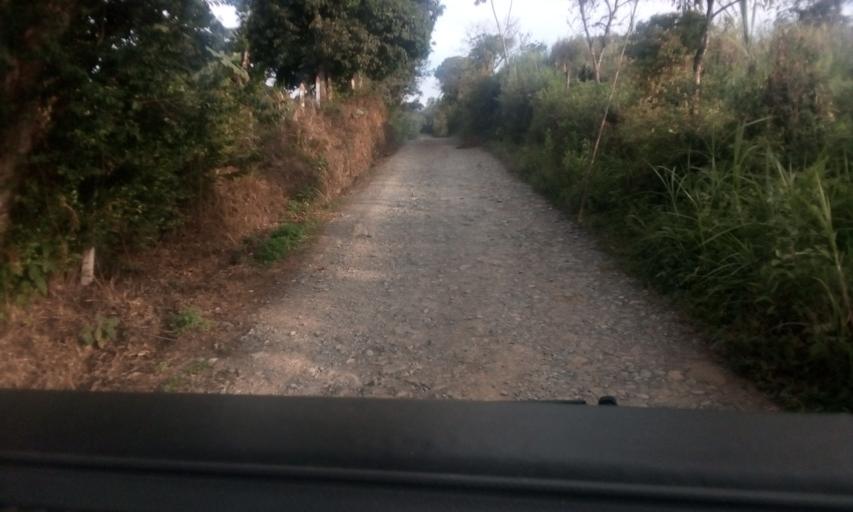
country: CO
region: Boyaca
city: Santana
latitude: 6.0252
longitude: -73.5166
